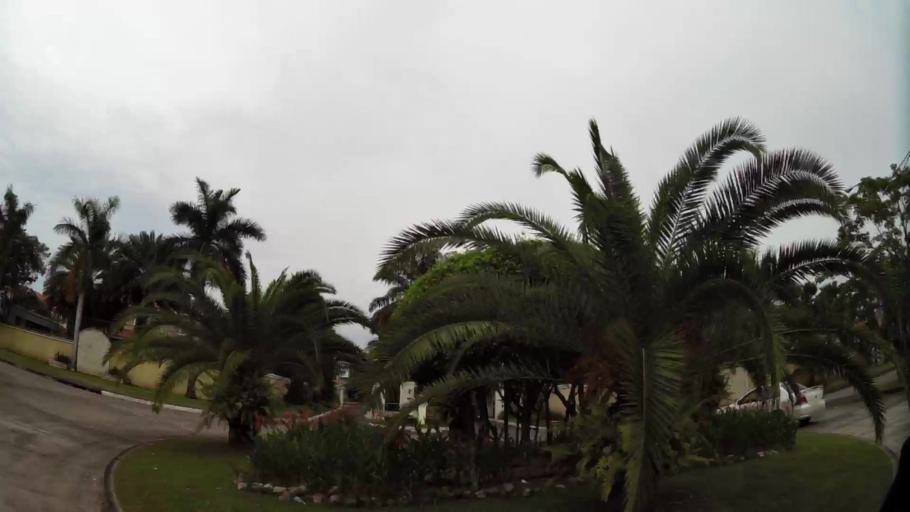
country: PA
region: Panama
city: San Miguelito
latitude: 9.0173
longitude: -79.4586
